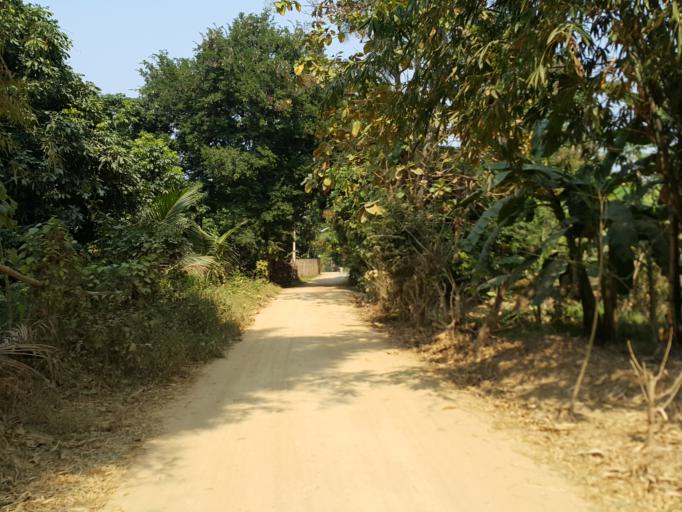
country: TH
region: Sukhothai
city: Thung Saliam
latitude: 17.3228
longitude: 99.5125
